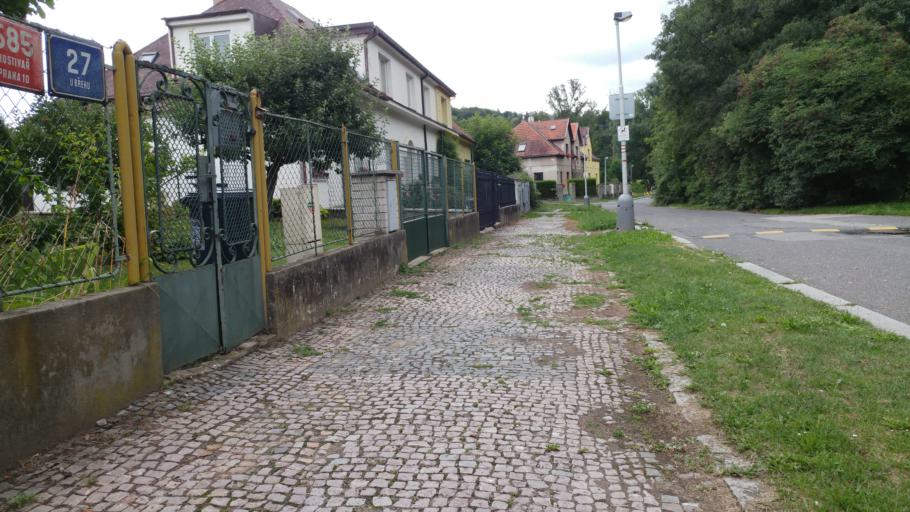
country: CZ
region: Praha
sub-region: Praha 14
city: Hostavice
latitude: 50.0504
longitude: 14.5313
